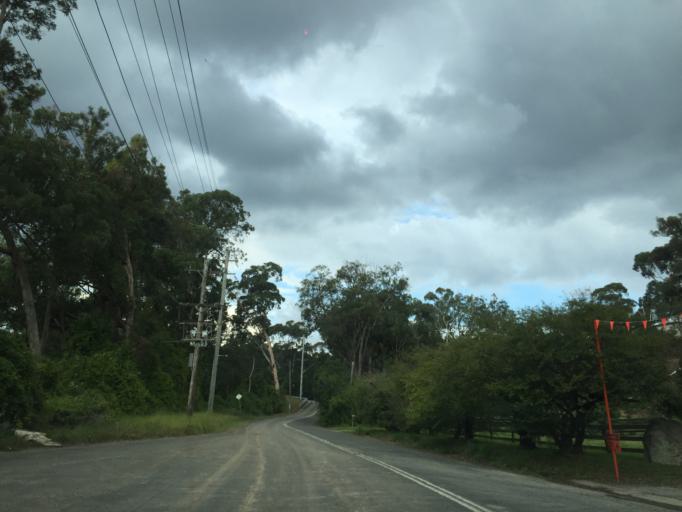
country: AU
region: New South Wales
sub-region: The Hills Shire
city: Beaumont Hills
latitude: -33.6931
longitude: 150.9686
